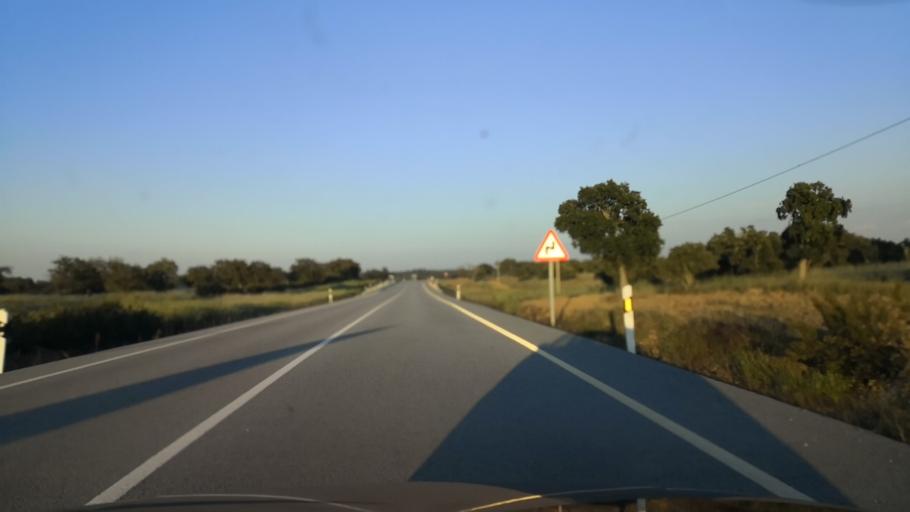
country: ES
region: Extremadura
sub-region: Provincia de Caceres
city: Salorino
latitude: 39.5107
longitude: -7.1055
